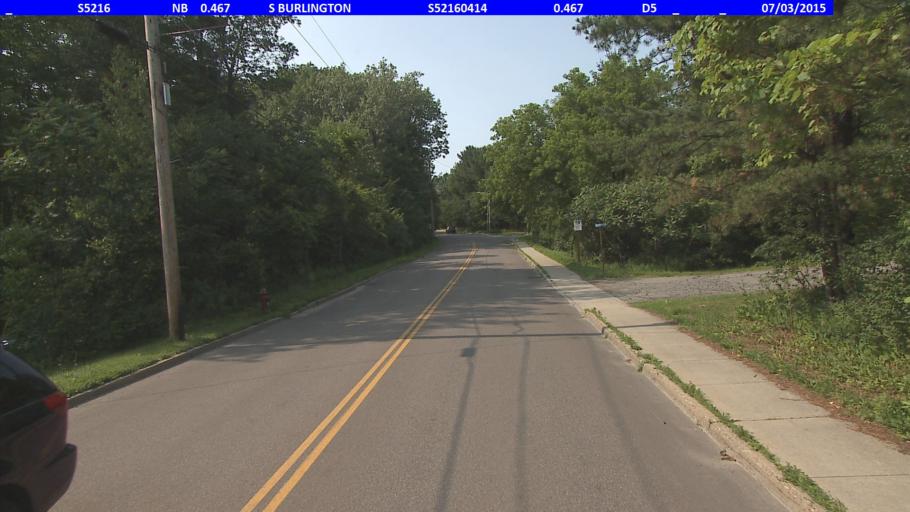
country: US
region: Vermont
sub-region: Chittenden County
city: South Burlington
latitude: 44.4736
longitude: -73.1726
